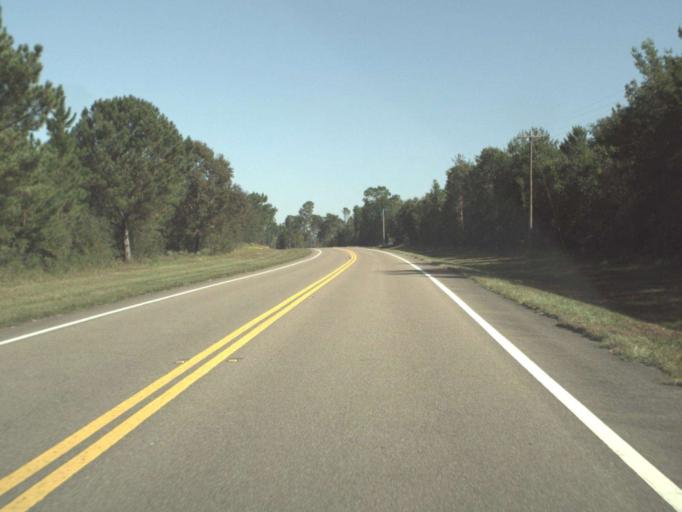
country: US
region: Florida
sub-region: Walton County
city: Freeport
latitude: 30.5439
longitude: -85.9173
